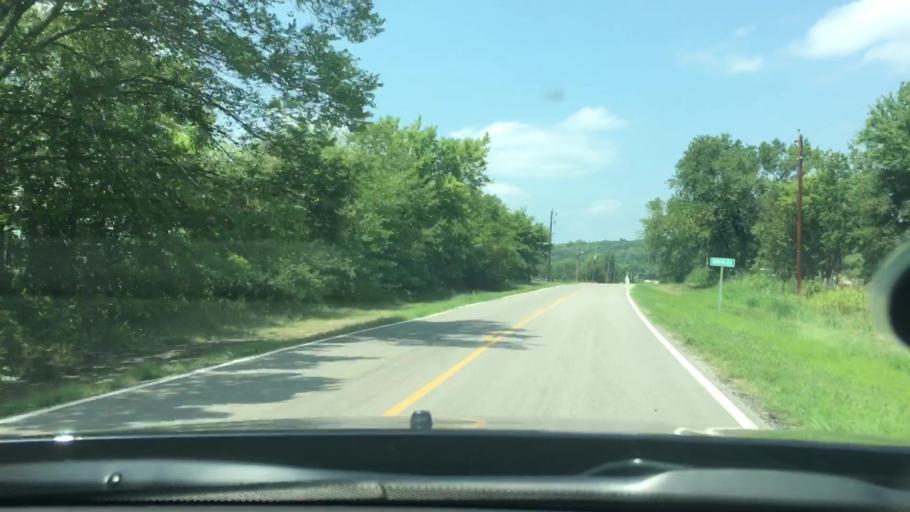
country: US
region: Oklahoma
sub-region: Johnston County
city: Tishomingo
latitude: 34.4117
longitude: -96.4969
